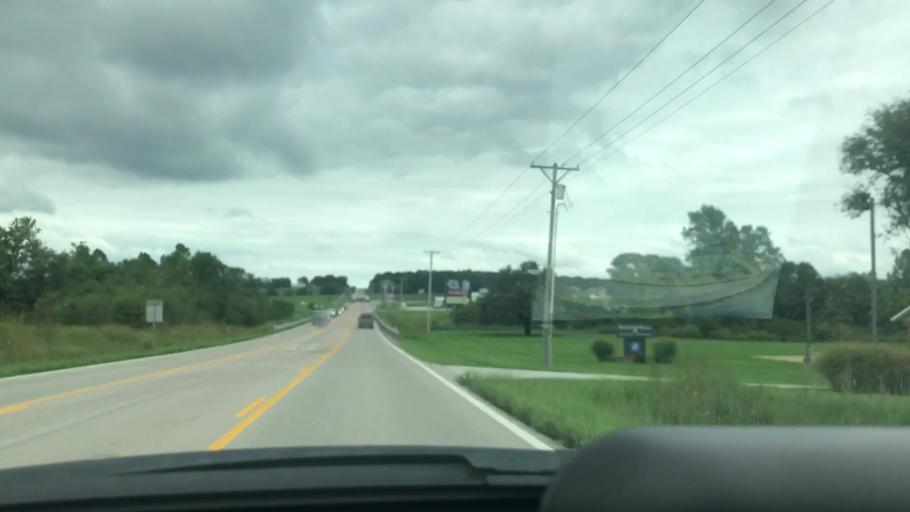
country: US
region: Missouri
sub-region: Dallas County
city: Buffalo
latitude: 37.6630
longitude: -93.1035
